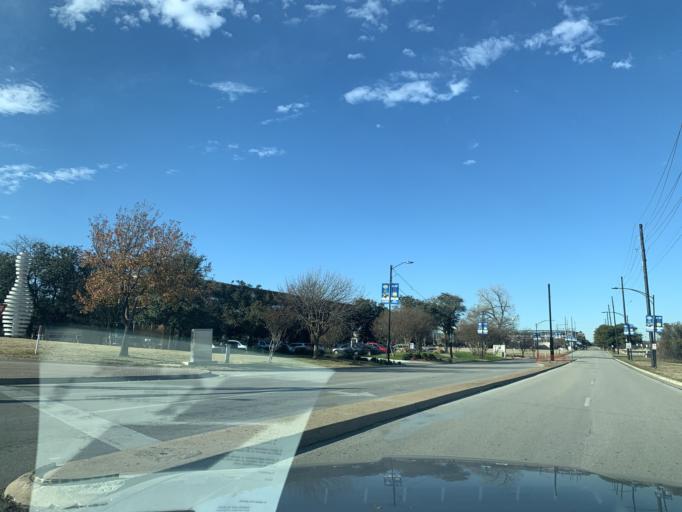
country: US
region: Texas
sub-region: Tarrant County
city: Arlington
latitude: 32.7525
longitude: -97.0681
